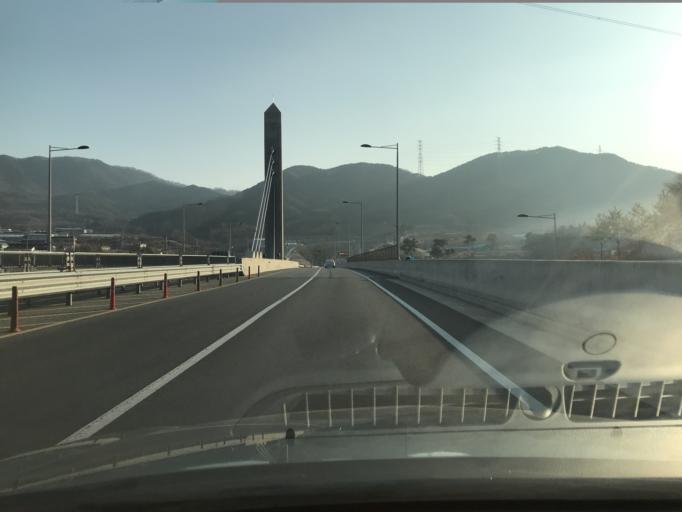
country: KR
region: Daegu
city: Hwawon
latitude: 35.7476
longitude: 128.4914
